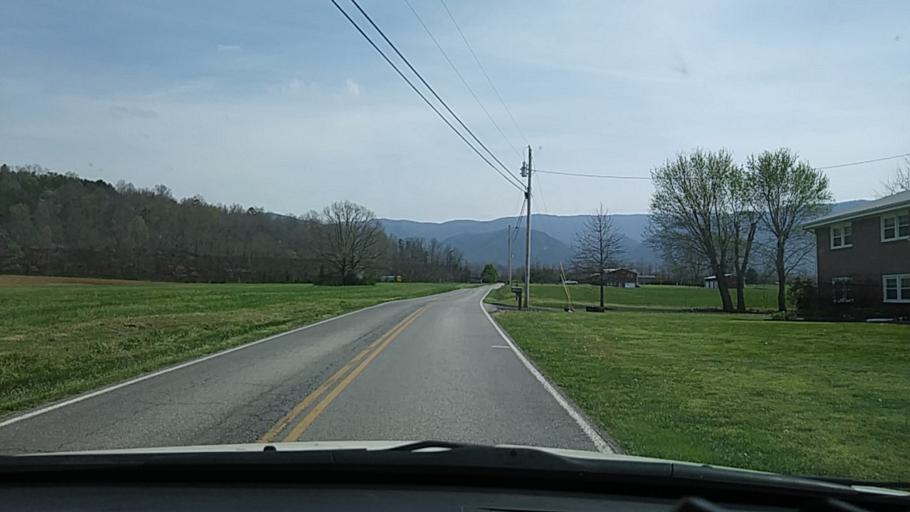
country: US
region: Tennessee
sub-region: Greene County
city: Tusculum
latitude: 36.0990
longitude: -82.7404
